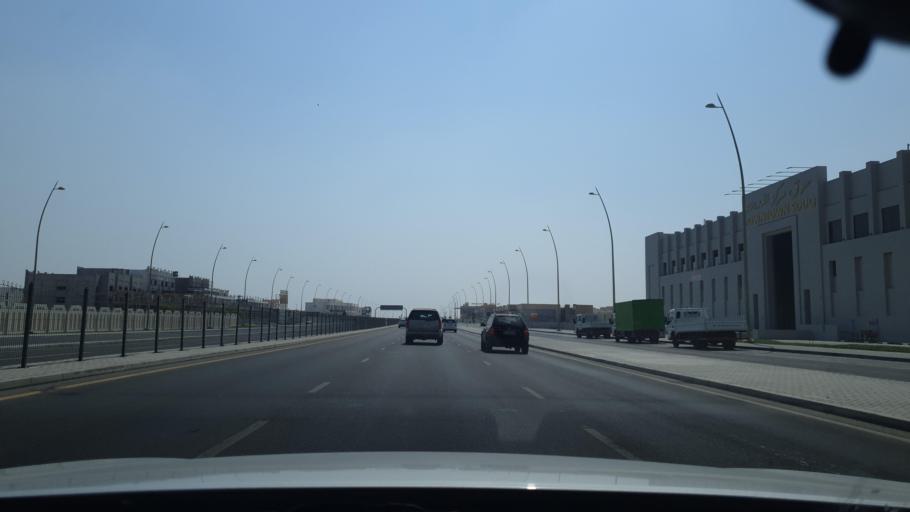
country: QA
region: Al Khawr
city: Al Khawr
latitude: 25.6726
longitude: 51.5009
